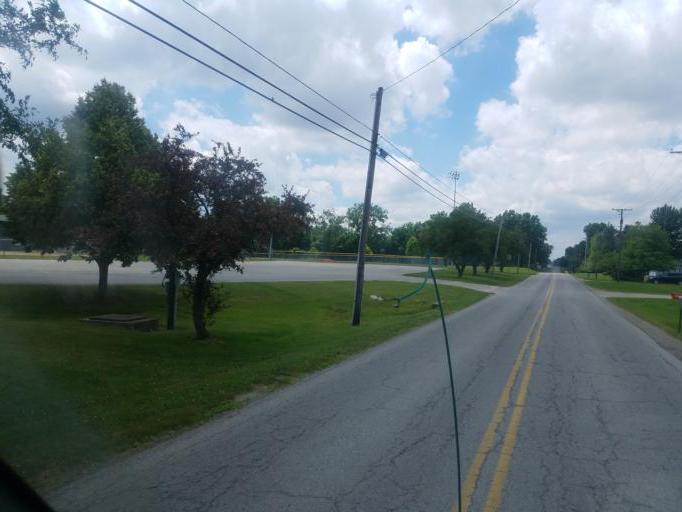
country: US
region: Ohio
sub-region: Huron County
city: Willard
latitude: 41.0545
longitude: -82.7387
